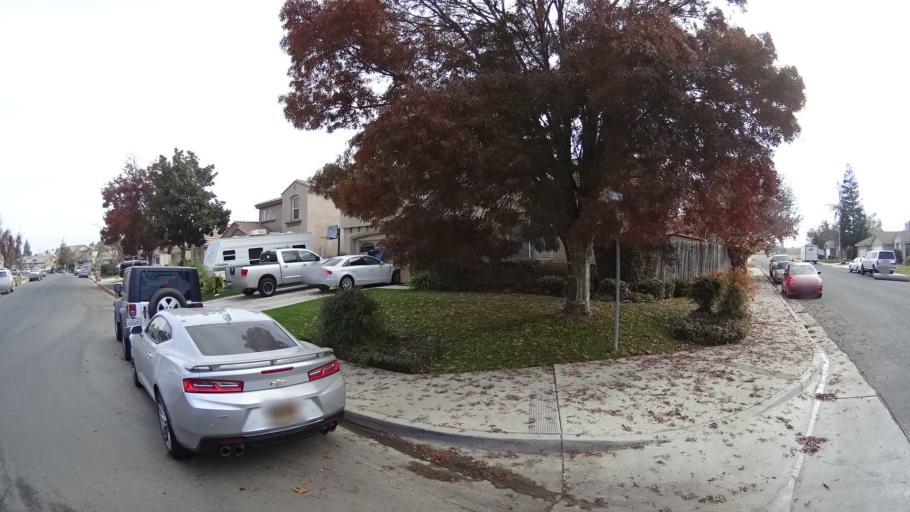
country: US
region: California
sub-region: Kern County
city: Rosedale
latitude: 35.3882
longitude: -119.1318
